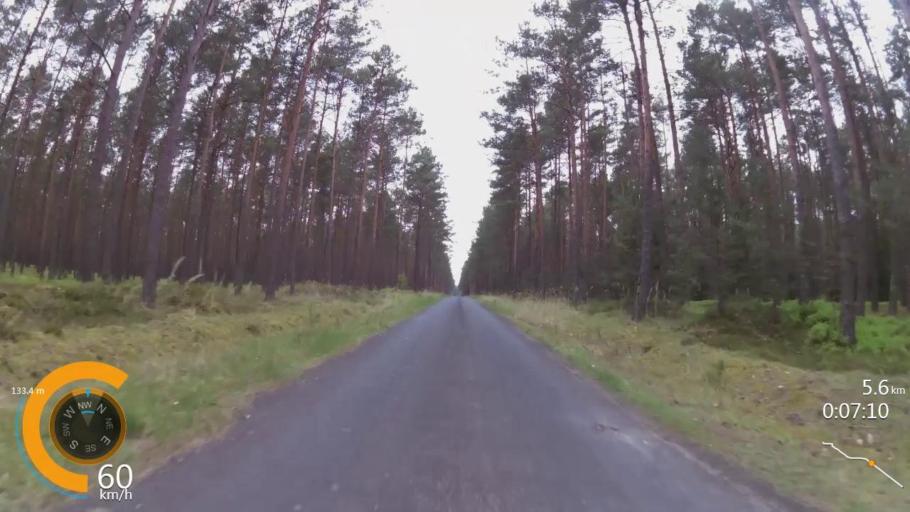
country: PL
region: West Pomeranian Voivodeship
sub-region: Powiat drawski
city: Wierzchowo
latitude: 53.4950
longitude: 16.1643
